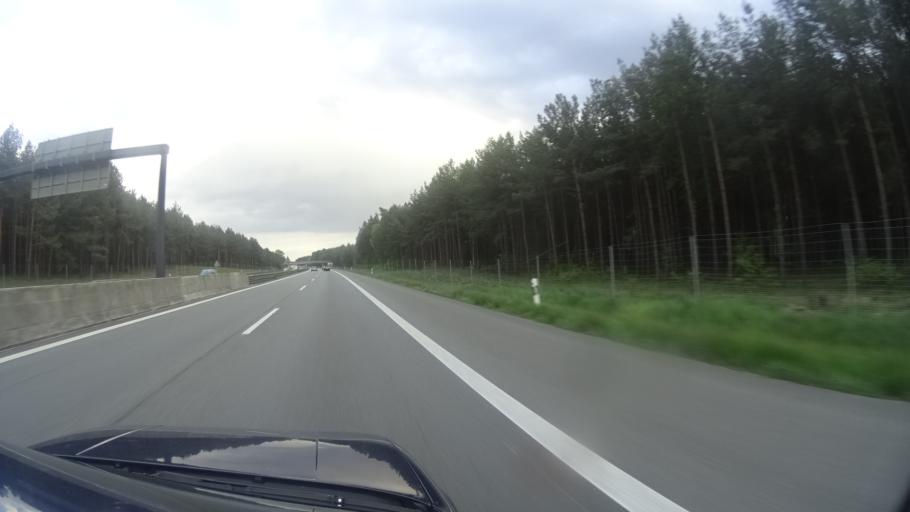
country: DE
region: Brandenburg
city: Wittstock
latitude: 53.1067
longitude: 12.4790
